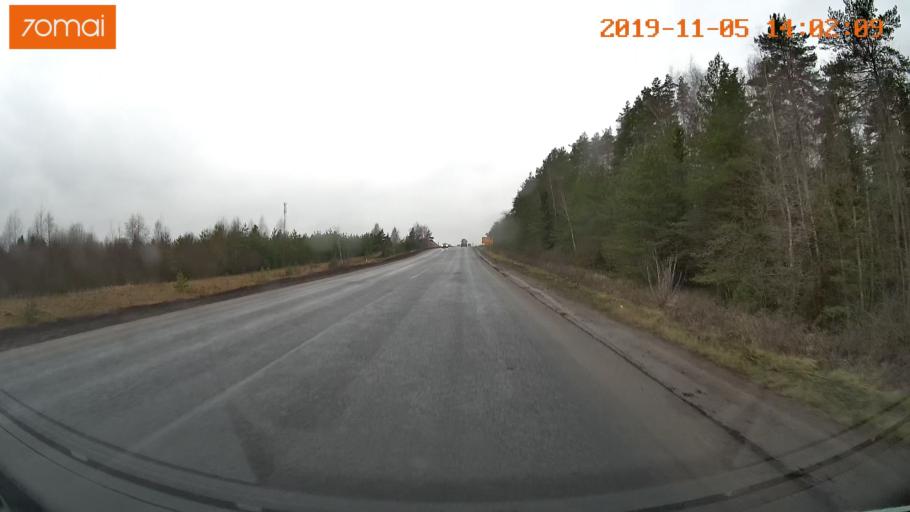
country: RU
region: Ivanovo
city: Kokhma
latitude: 57.0040
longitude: 41.2188
